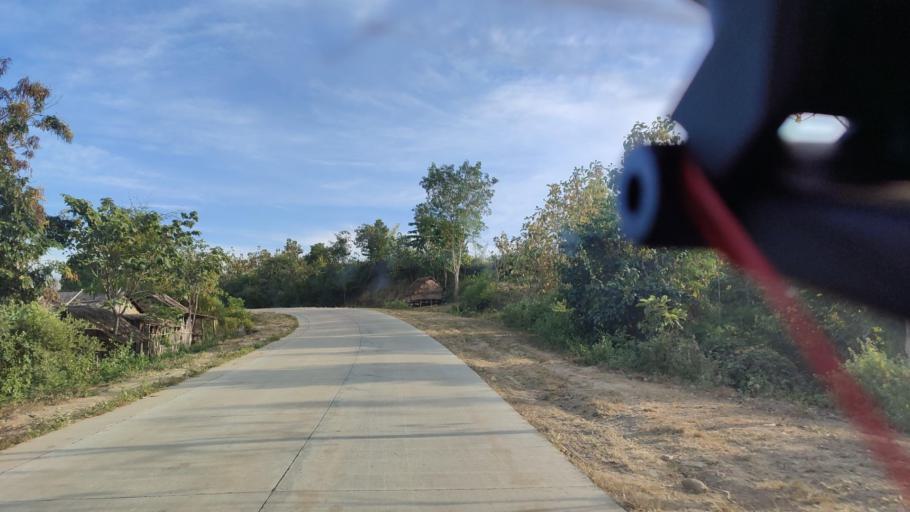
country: MM
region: Magway
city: Taungdwingyi
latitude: 20.0376
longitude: 95.7853
